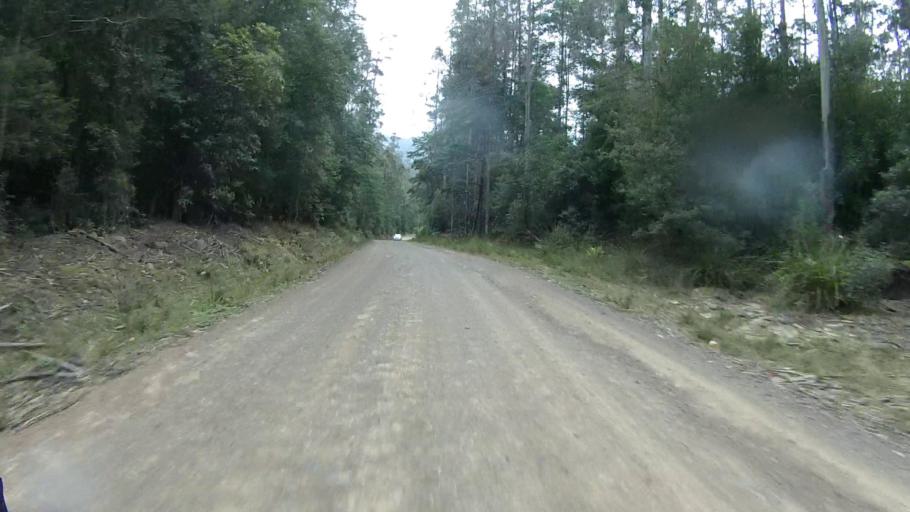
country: AU
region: Tasmania
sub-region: Sorell
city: Sorell
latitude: -42.7088
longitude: 147.8401
